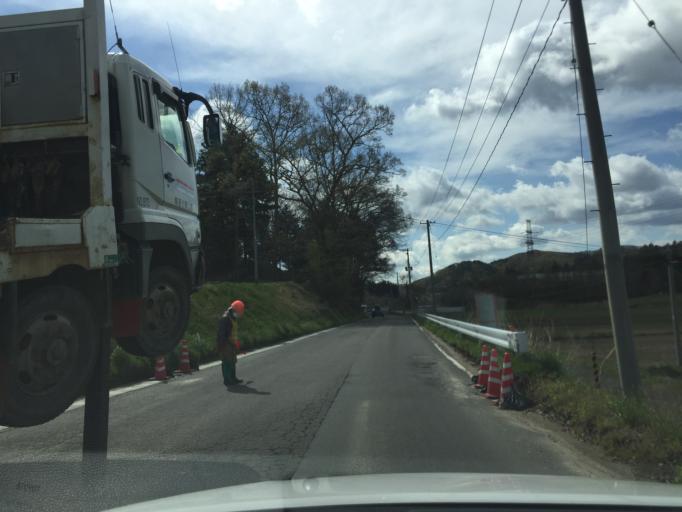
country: JP
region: Fukushima
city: Funehikimachi-funehiki
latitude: 37.6161
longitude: 140.6529
